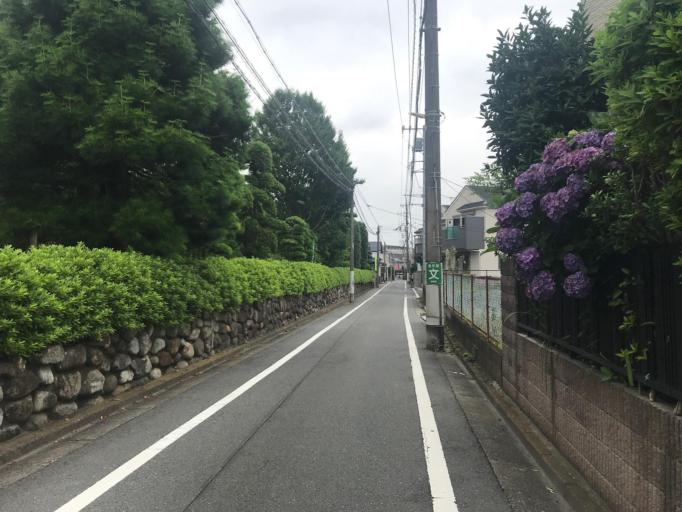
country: JP
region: Saitama
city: Wako
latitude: 35.7341
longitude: 139.6194
